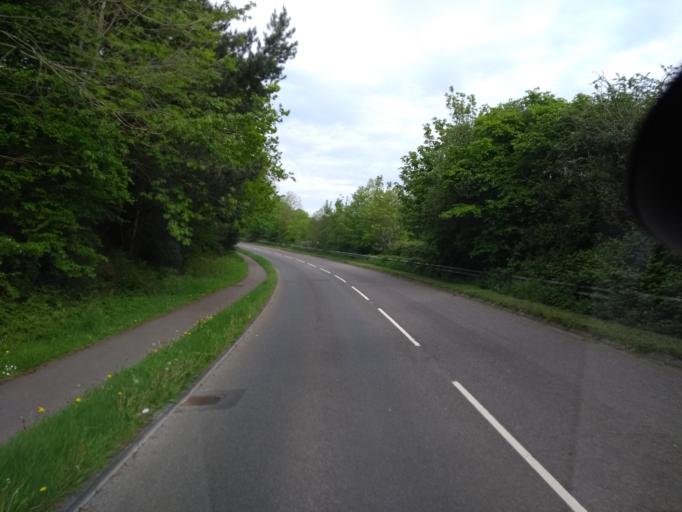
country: GB
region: England
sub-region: Dorset
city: Lyme Regis
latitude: 50.7411
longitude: -2.9156
